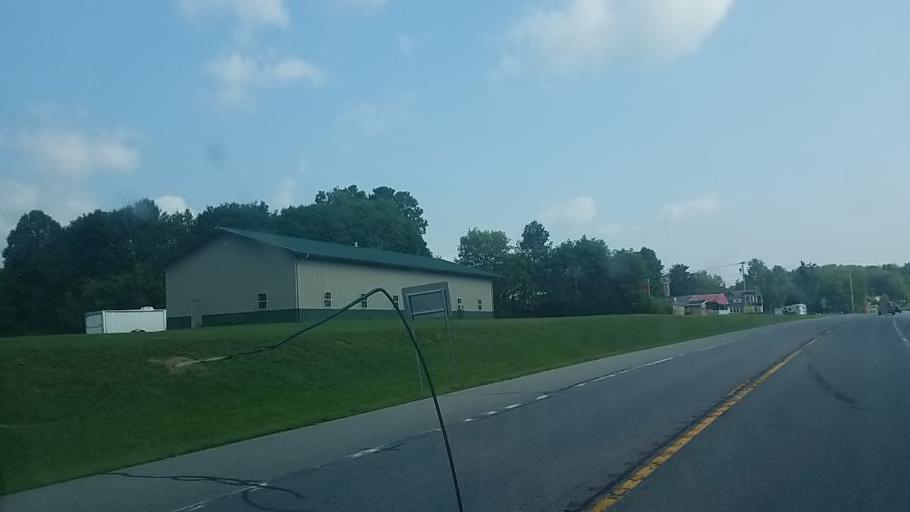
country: US
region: New York
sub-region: Fulton County
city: Gloversville
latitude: 43.1004
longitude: -74.2760
